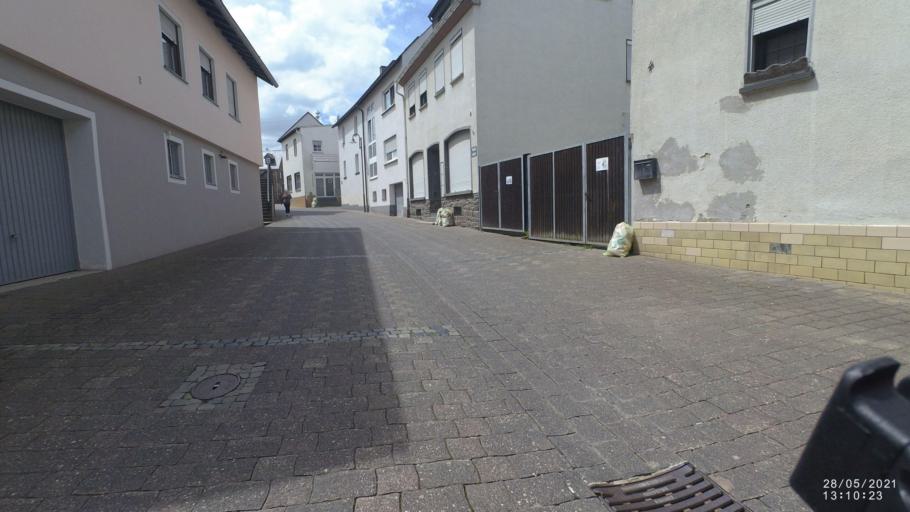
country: DE
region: Rheinland-Pfalz
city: Pillig
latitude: 50.2397
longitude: 7.3117
